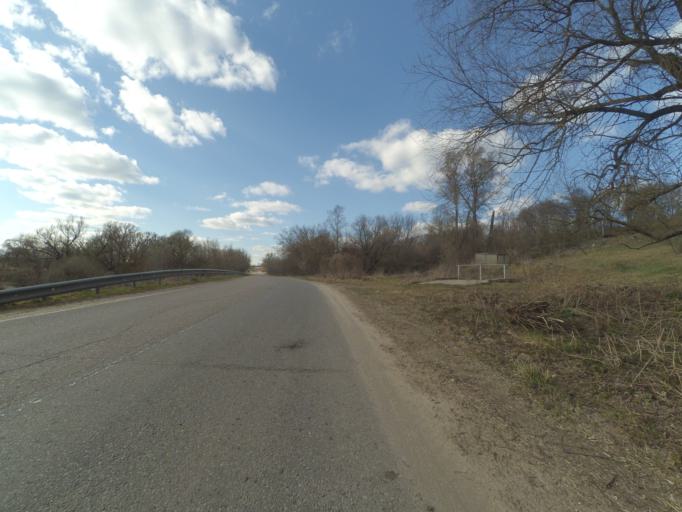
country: RU
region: Moskovskaya
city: Bol'shoye Gryzlovo
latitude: 54.8758
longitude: 37.8222
